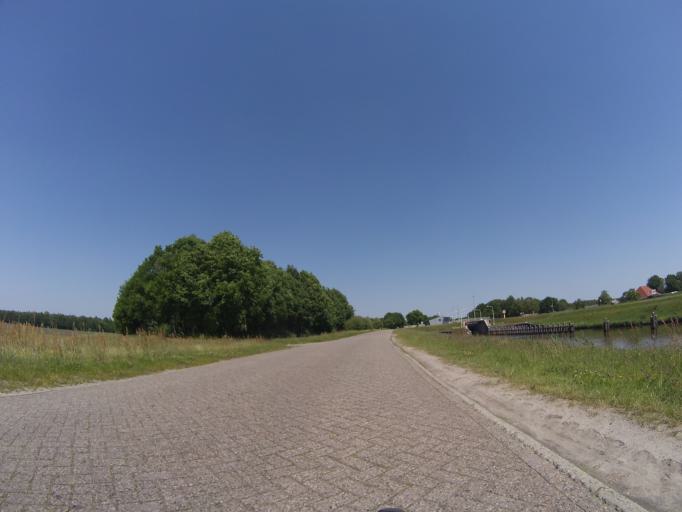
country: NL
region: Drenthe
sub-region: Gemeente Emmen
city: Schoonebeek
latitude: 52.6887
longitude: 6.8524
